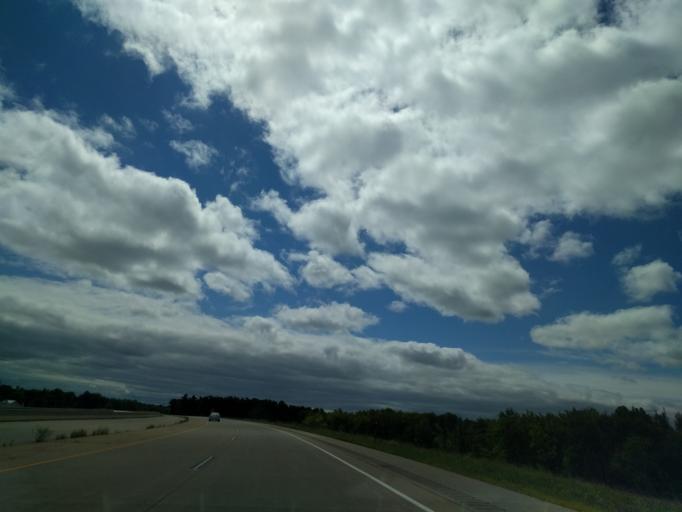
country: US
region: Wisconsin
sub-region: Oconto County
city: Oconto
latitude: 44.8951
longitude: -87.8996
